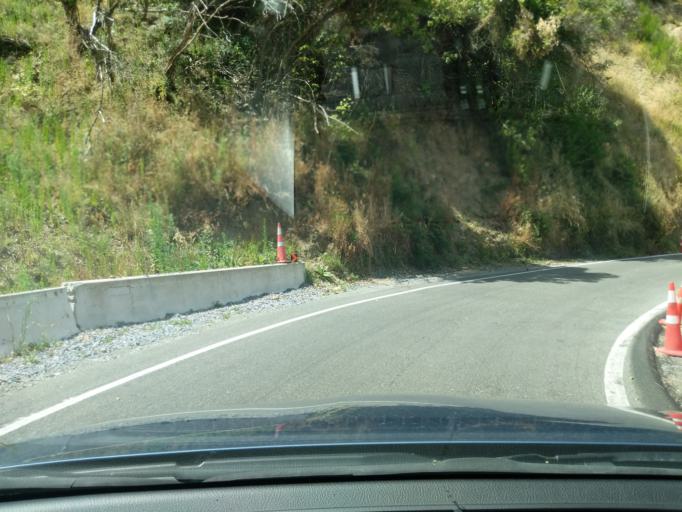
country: NZ
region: Tasman
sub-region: Tasman District
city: Motueka
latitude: -41.0458
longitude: 172.9559
